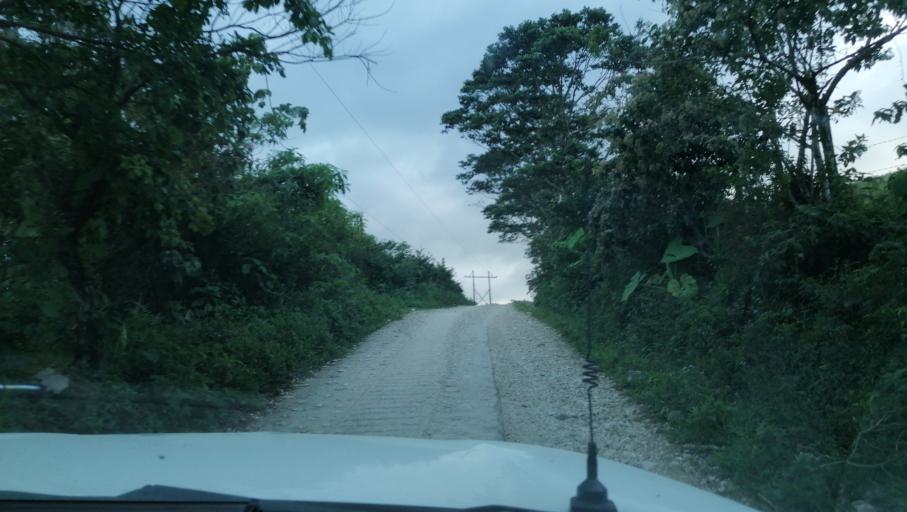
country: MX
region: Chiapas
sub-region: Francisco Leon
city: San Miguel la Sardina
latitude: 17.2939
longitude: -93.2678
